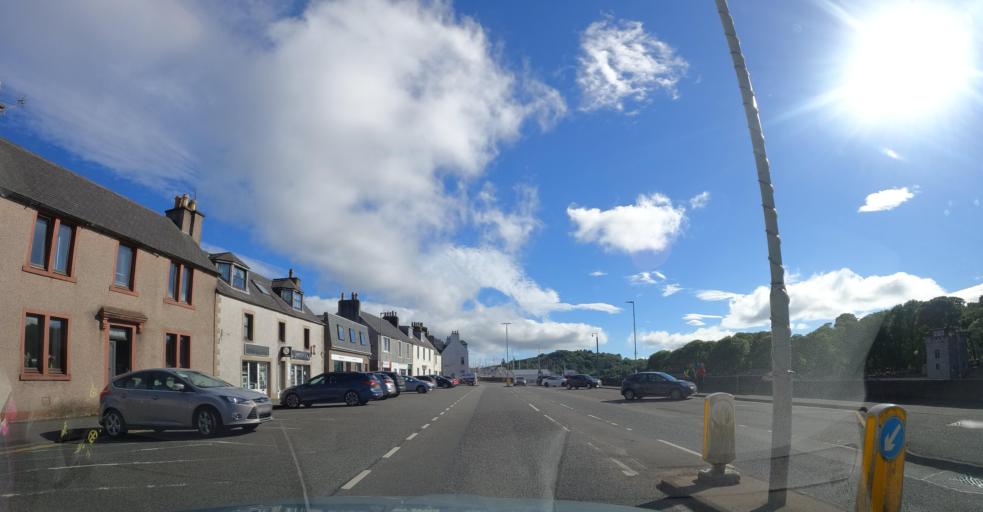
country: GB
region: Scotland
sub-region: Eilean Siar
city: Stornoway
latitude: 58.2120
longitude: -6.3881
